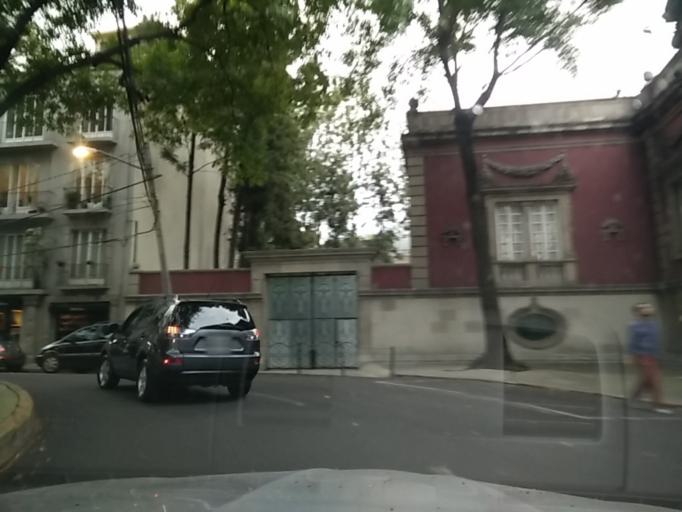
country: MX
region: Mexico City
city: Benito Juarez
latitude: 19.4207
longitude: -99.1609
